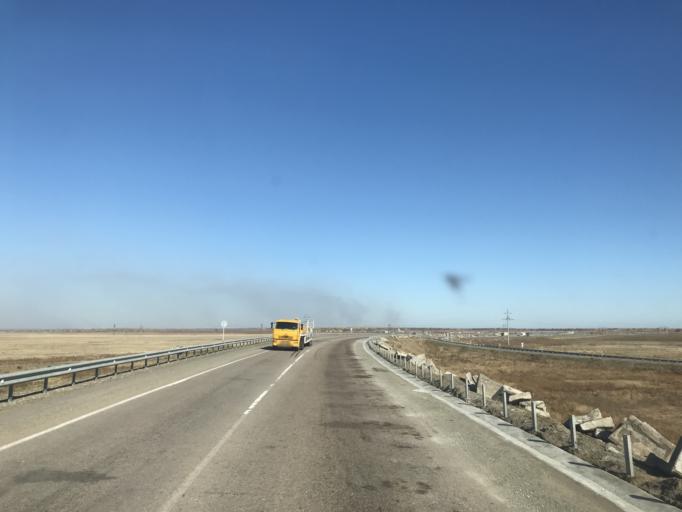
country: KZ
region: Pavlodar
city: Leninskiy
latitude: 52.1538
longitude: 76.8220
